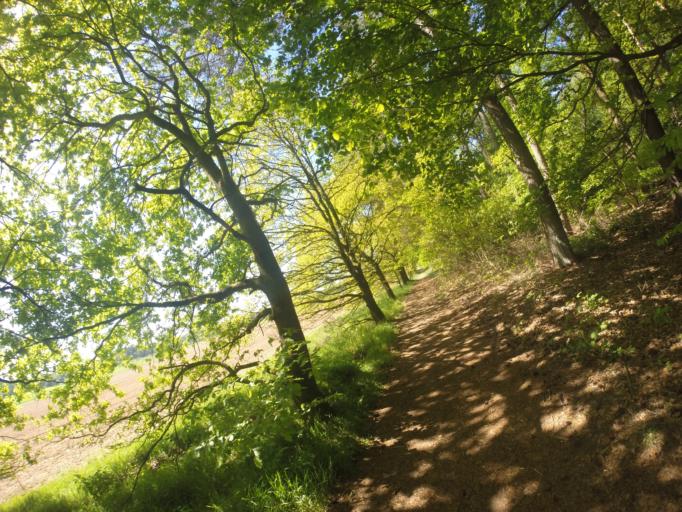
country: NL
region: Gelderland
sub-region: Gemeente Montferland
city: s-Heerenberg
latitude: 51.9062
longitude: 6.2436
